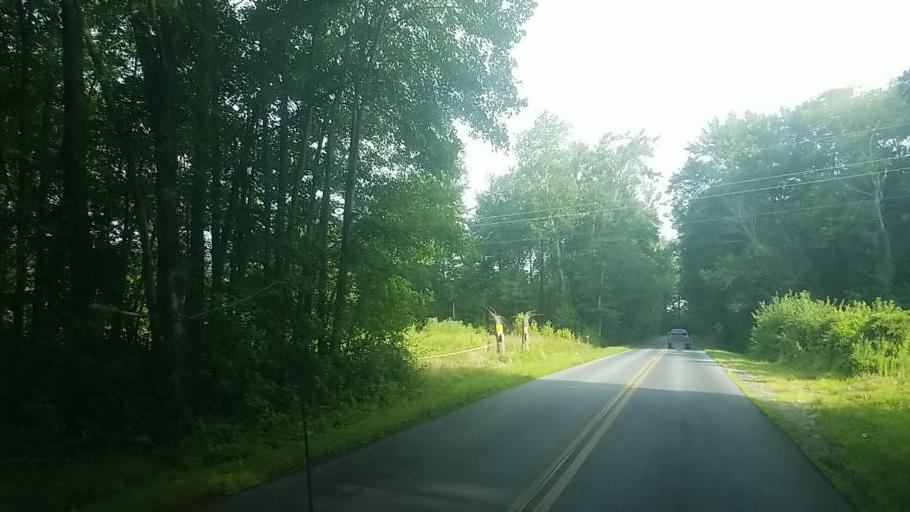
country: US
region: Maryland
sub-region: Worcester County
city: West Ocean City
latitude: 38.3283
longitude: -75.1549
